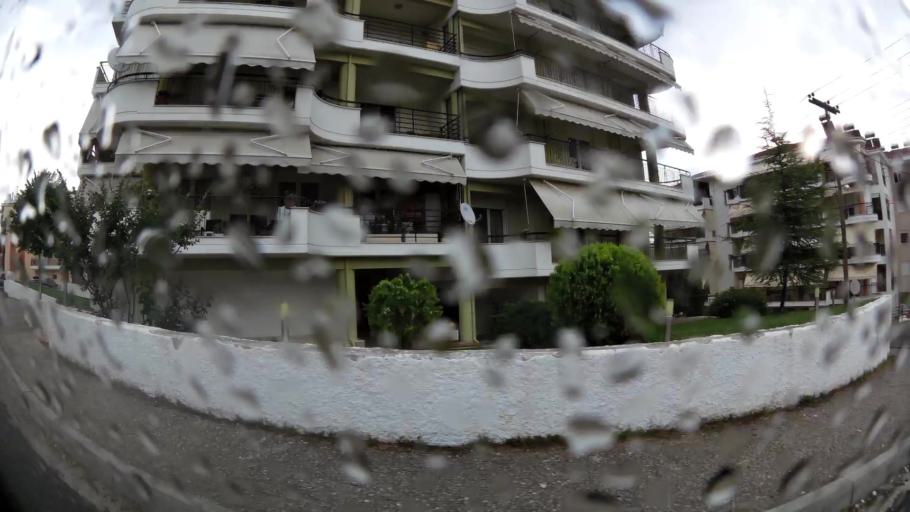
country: GR
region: Central Macedonia
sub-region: Nomos Imathias
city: Veroia
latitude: 40.5212
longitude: 22.1932
